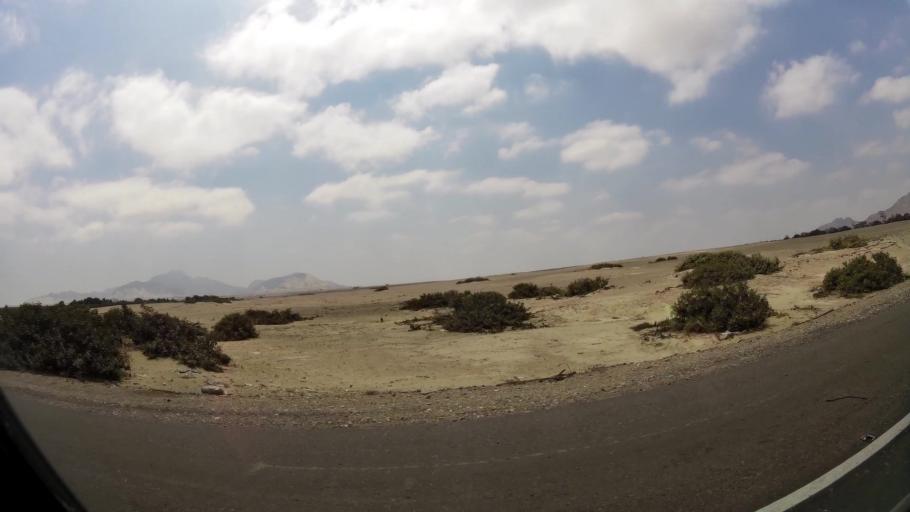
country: PE
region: La Libertad
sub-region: Ascope
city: Paijan
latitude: -7.6626
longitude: -79.3328
